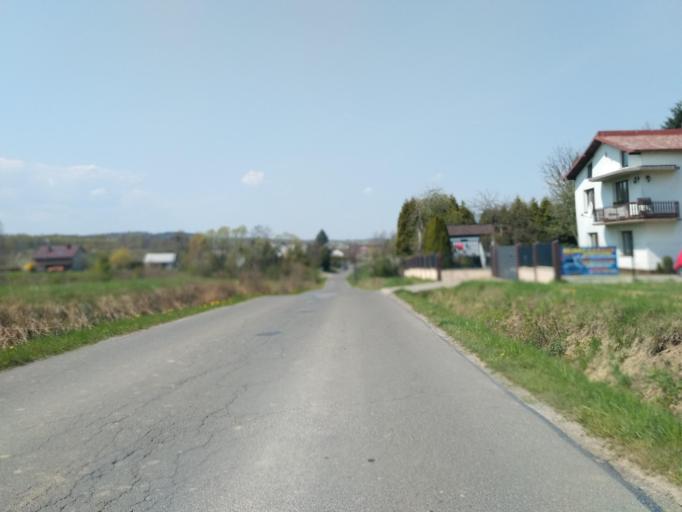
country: PL
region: Subcarpathian Voivodeship
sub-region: Powiat krosnienski
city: Chorkowka
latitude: 49.6637
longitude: 21.6292
